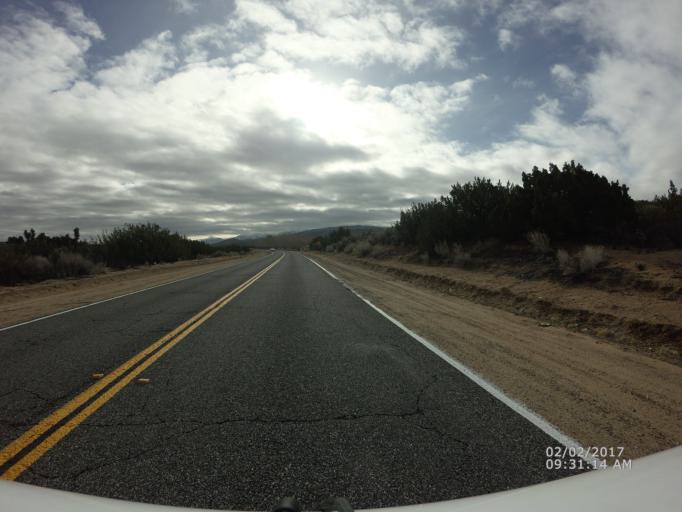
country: US
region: California
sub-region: Los Angeles County
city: Littlerock
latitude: 34.5163
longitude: -118.0335
